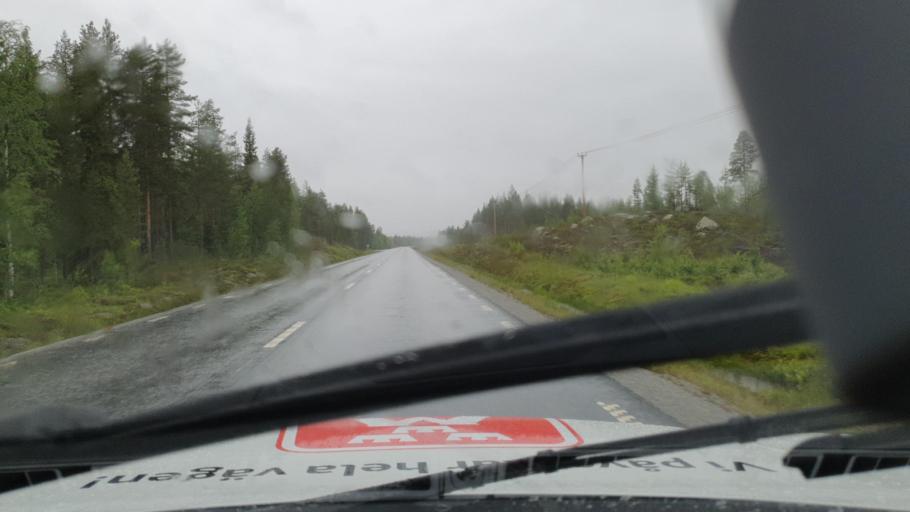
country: SE
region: Vaesternorrland
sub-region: OErnskoeldsviks Kommun
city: Bredbyn
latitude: 64.1141
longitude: 18.1125
